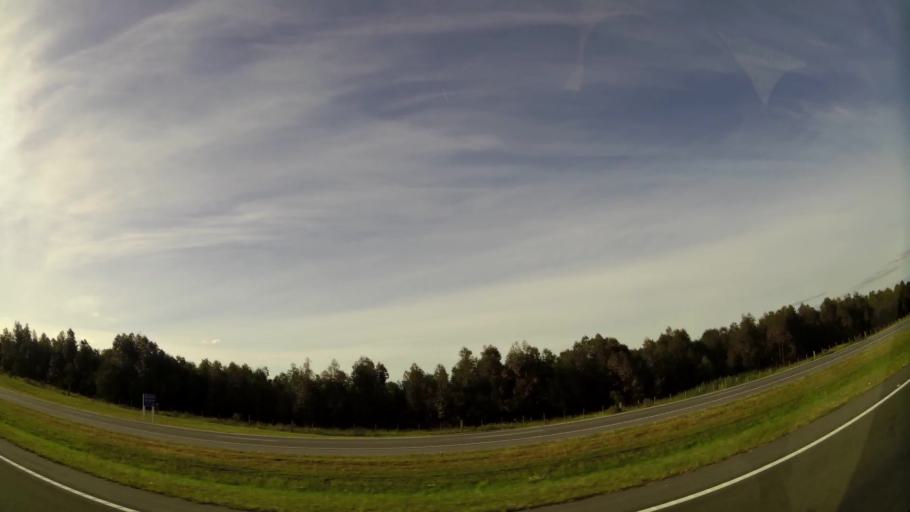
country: UY
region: Lavalleja
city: Solis de Mataojo
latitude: -34.7824
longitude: -55.4859
